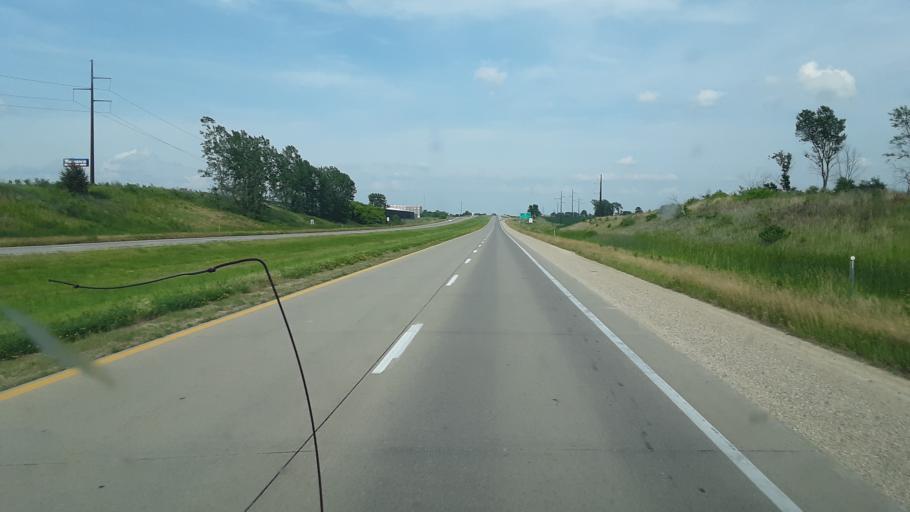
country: US
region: Iowa
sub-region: Marshall County
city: Marshalltown
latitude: 42.0035
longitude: -92.9262
